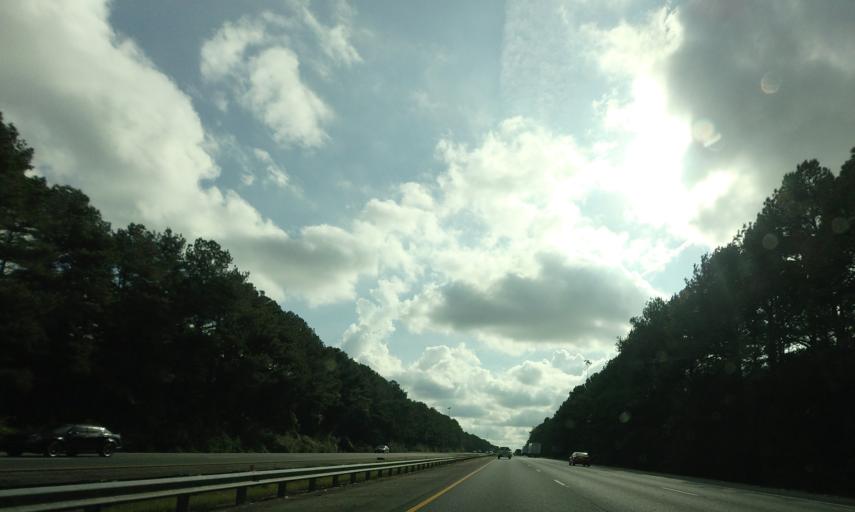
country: US
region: Georgia
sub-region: Houston County
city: Perry
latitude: 32.4845
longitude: -83.7425
